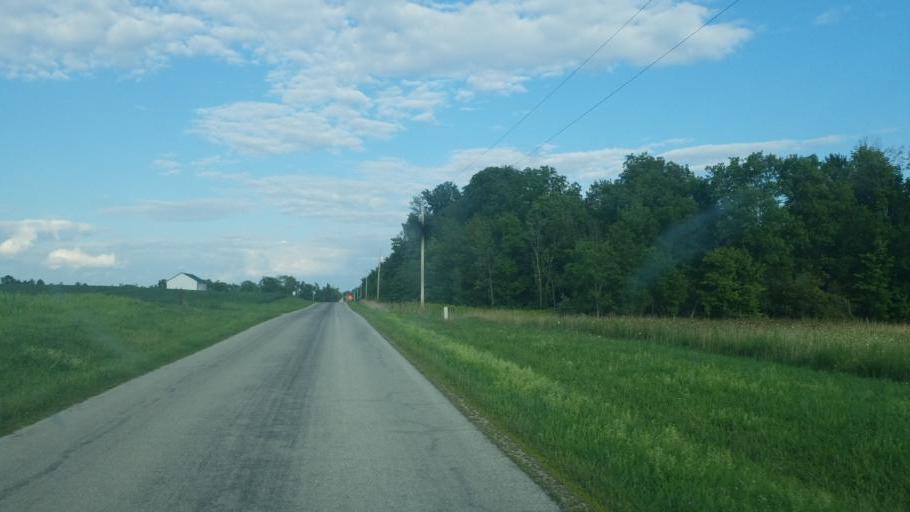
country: US
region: Ohio
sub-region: Seneca County
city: Tiffin
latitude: 41.1100
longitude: -83.0352
